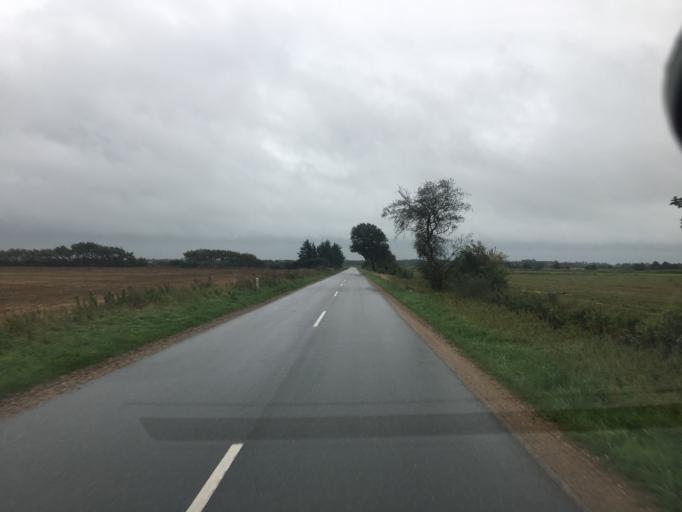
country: DK
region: South Denmark
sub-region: Tonder Kommune
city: Logumkloster
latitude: 54.9741
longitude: 9.0427
